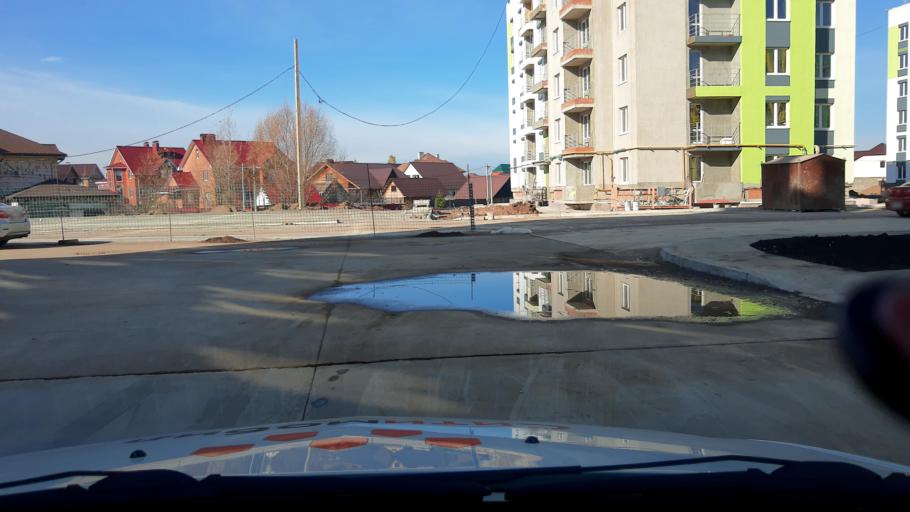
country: RU
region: Bashkortostan
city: Ufa
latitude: 54.7963
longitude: 55.9510
